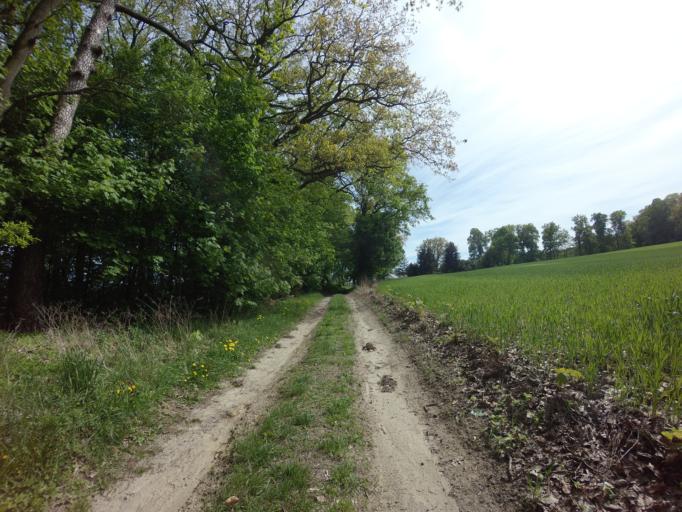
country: PL
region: West Pomeranian Voivodeship
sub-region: Powiat choszczenski
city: Bierzwnik
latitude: 53.1538
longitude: 15.6254
